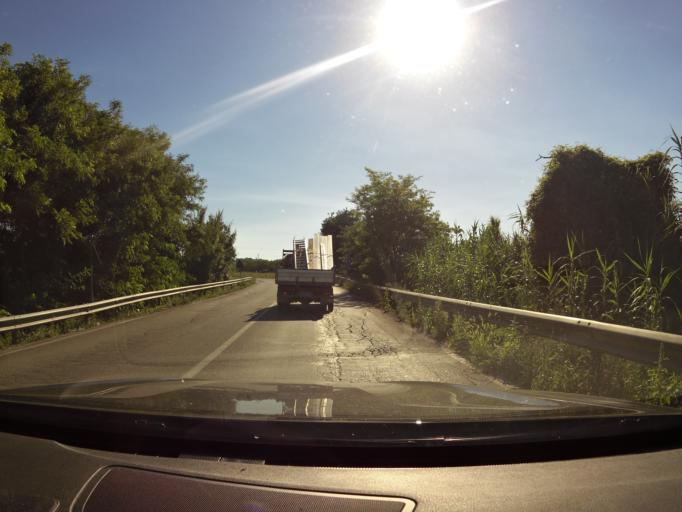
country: IT
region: The Marches
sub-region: Provincia di Ancona
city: Villa Musone
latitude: 43.4768
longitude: 13.5844
